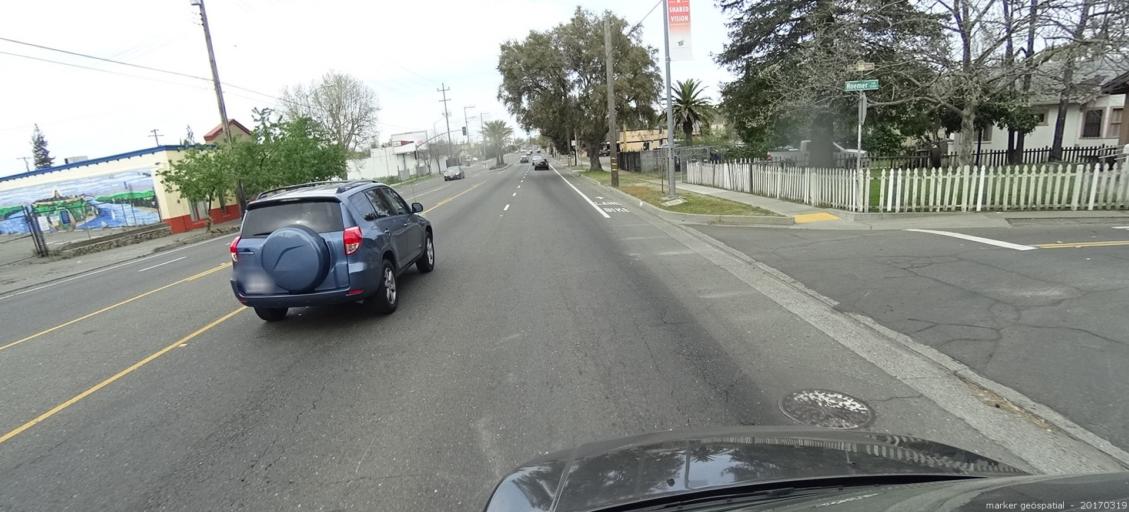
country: US
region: California
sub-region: Sacramento County
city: Parkway
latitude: 38.5358
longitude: -121.4476
